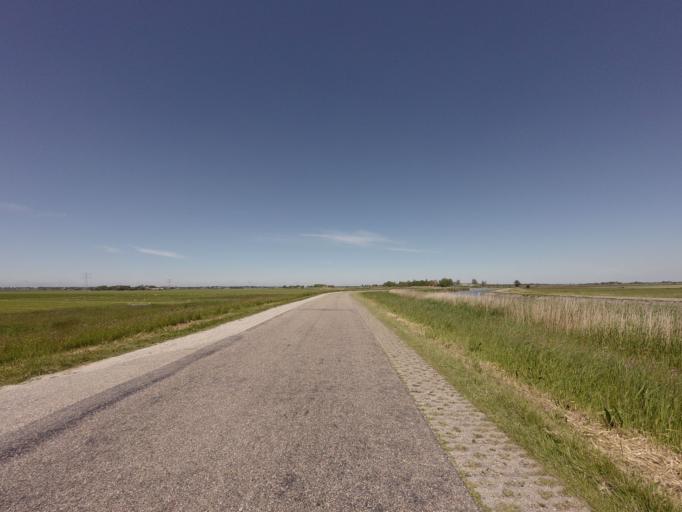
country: NL
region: North Holland
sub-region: Gemeente Alkmaar
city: Alkmaar
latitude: 52.5636
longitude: 4.7923
